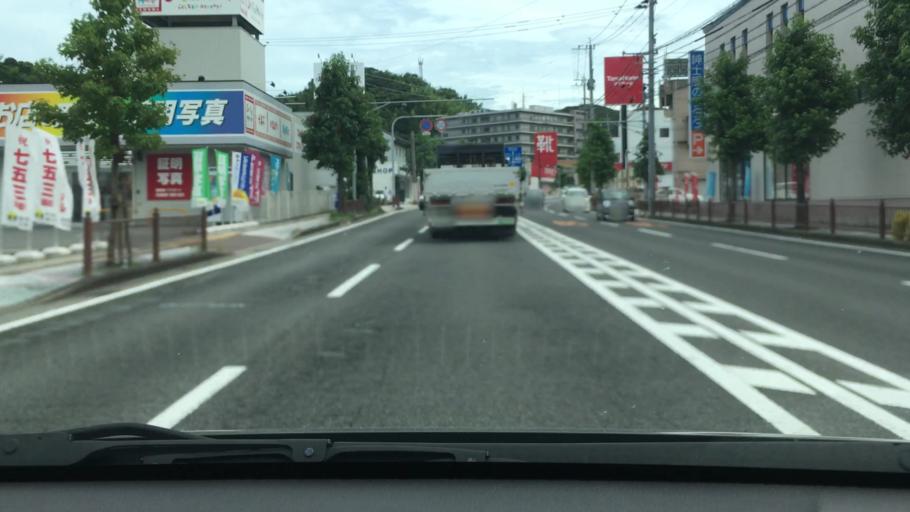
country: JP
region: Nagasaki
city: Togitsu
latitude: 32.8236
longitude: 129.8486
